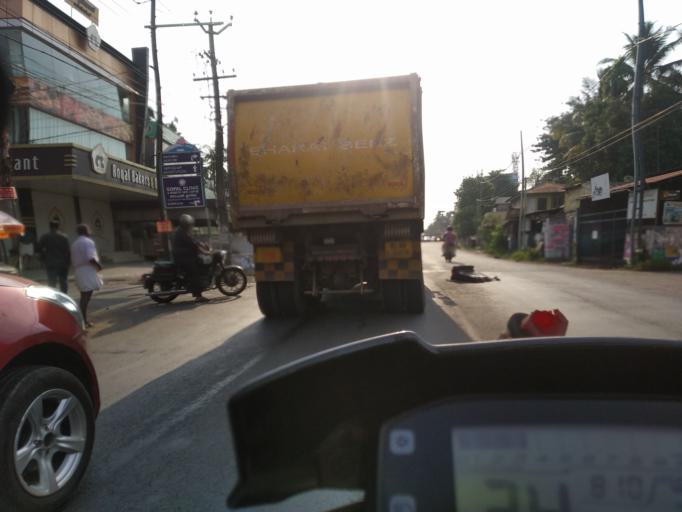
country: IN
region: Kerala
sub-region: Ernakulam
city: Cochin
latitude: 9.9541
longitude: 76.3437
